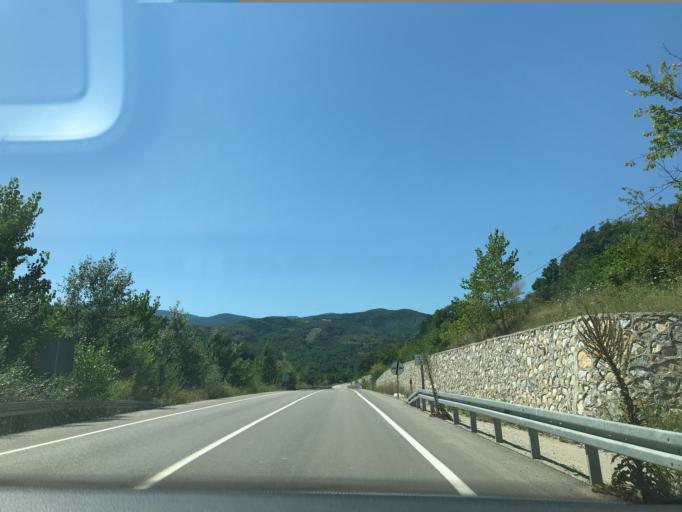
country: TR
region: Bursa
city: Tahtakopru
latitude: 39.9676
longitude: 29.6046
